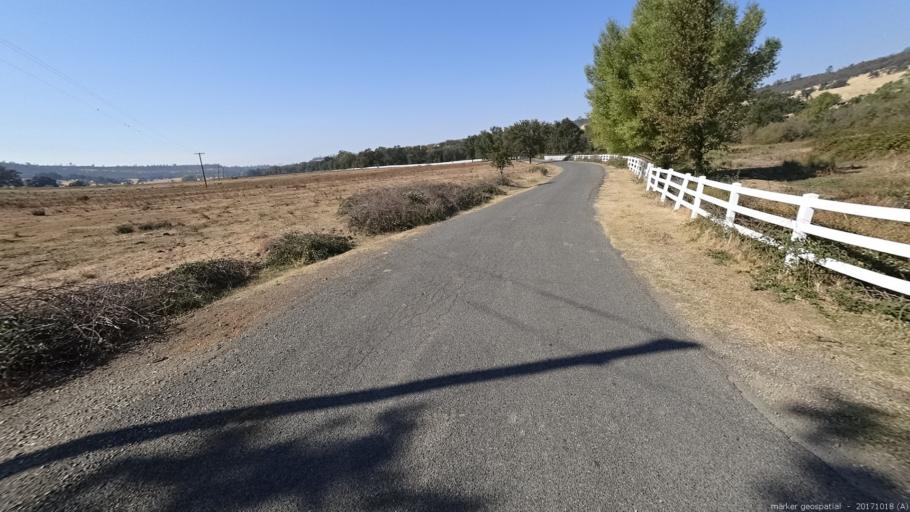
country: US
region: California
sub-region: Shasta County
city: Palo Cedro
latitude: 40.5523
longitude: -122.0639
